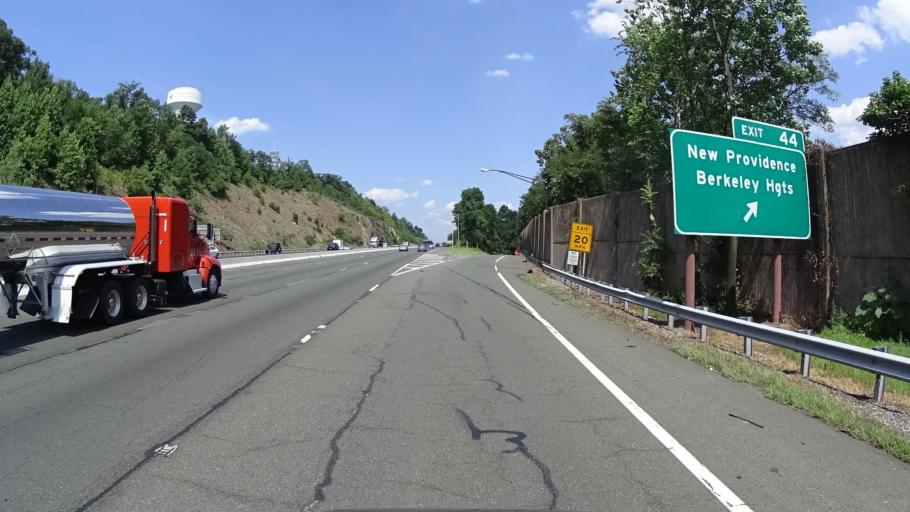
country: US
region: New Jersey
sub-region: Union County
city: New Providence
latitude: 40.6790
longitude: -74.3978
